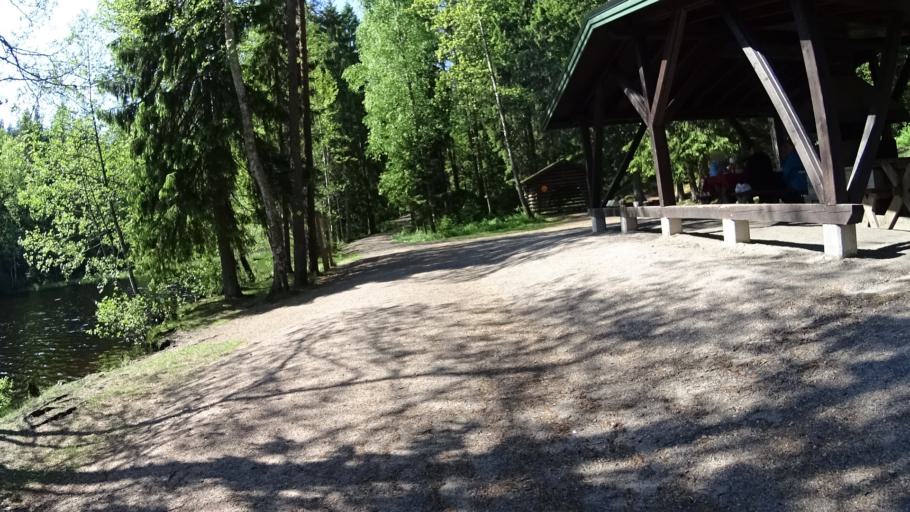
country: FI
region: Uusimaa
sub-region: Helsinki
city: Espoo
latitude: 60.3292
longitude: 24.6657
